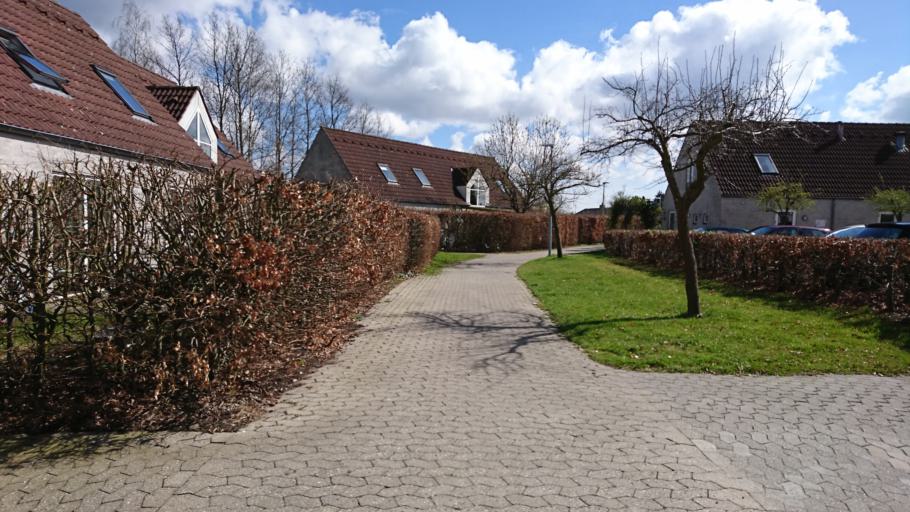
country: DK
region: Capital Region
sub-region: Egedal Kommune
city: Ganlose
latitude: 55.7902
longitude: 12.2685
